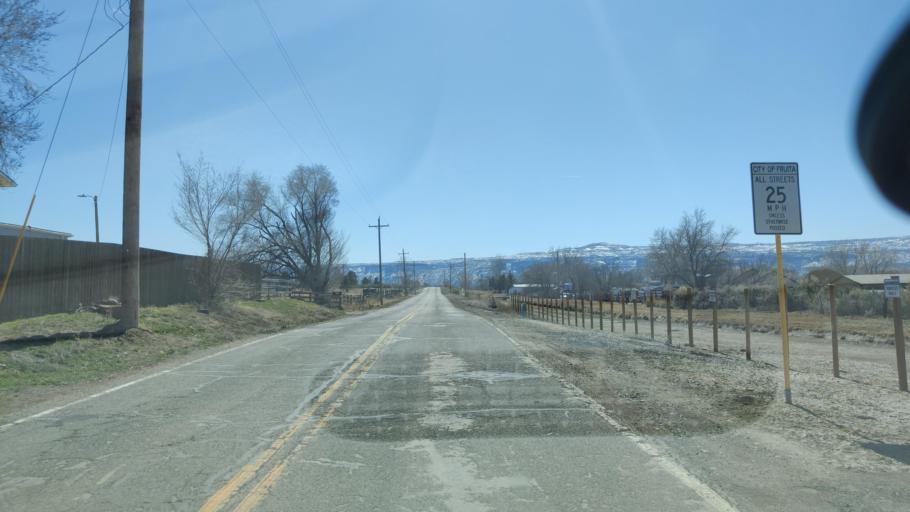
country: US
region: Colorado
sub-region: Mesa County
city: Fruita
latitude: 39.1776
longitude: -108.7105
